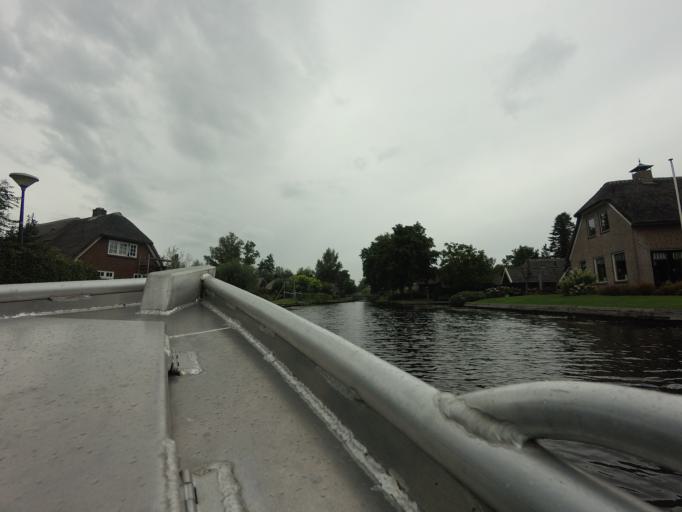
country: NL
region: Overijssel
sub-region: Gemeente Steenwijkerland
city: Giethoorn
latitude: 52.7228
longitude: 6.0372
